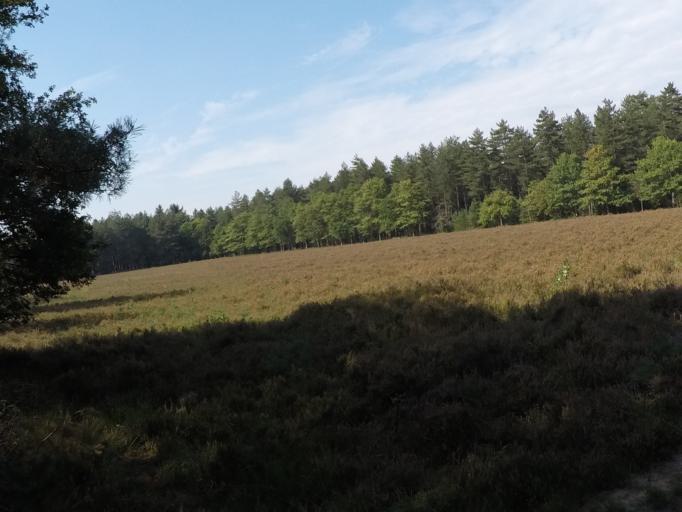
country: BE
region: Flanders
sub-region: Provincie Antwerpen
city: Kapellen
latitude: 51.3414
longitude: 4.4304
